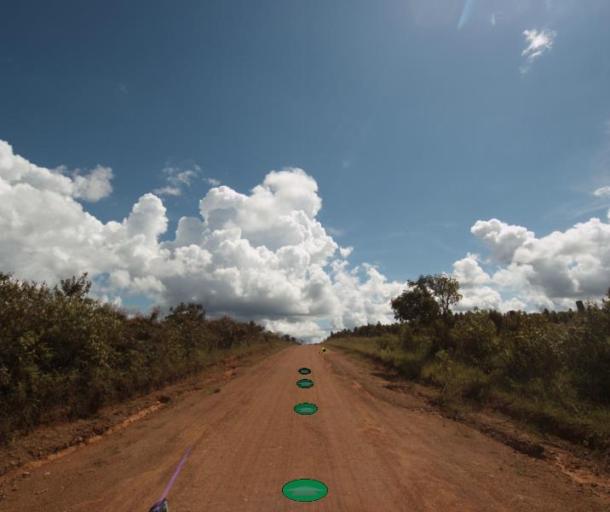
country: BR
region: Goias
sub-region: Pirenopolis
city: Pirenopolis
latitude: -15.7811
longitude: -48.8184
